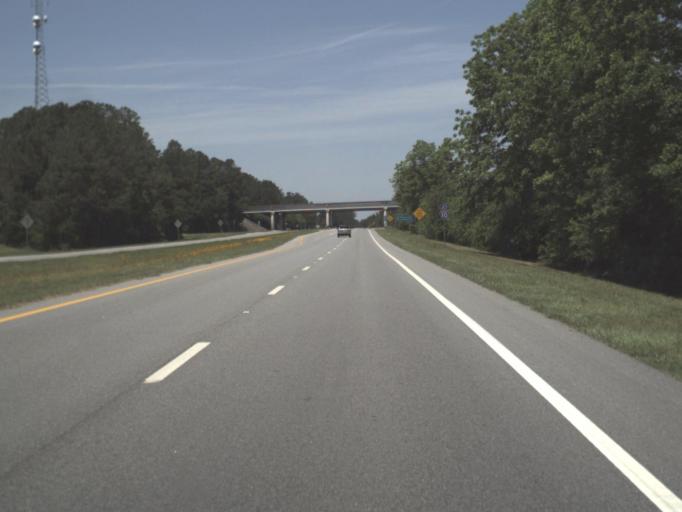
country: US
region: Florida
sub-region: Suwannee County
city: Live Oak
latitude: 30.3420
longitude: -83.0869
